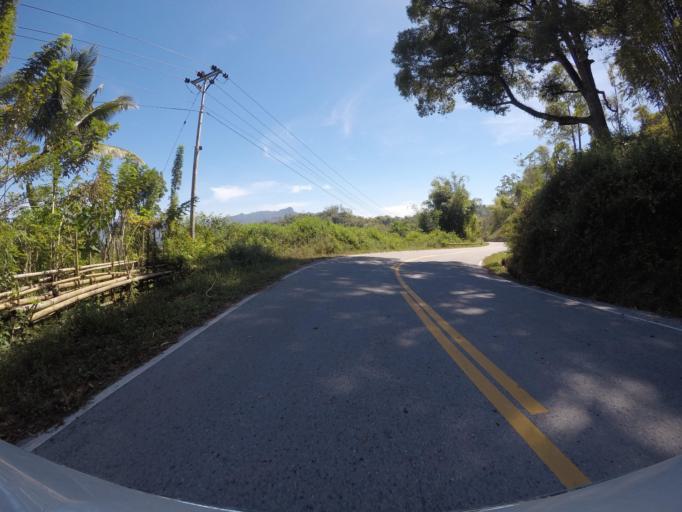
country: TL
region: Manufahi
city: Same
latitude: -8.8832
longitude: 125.9881
